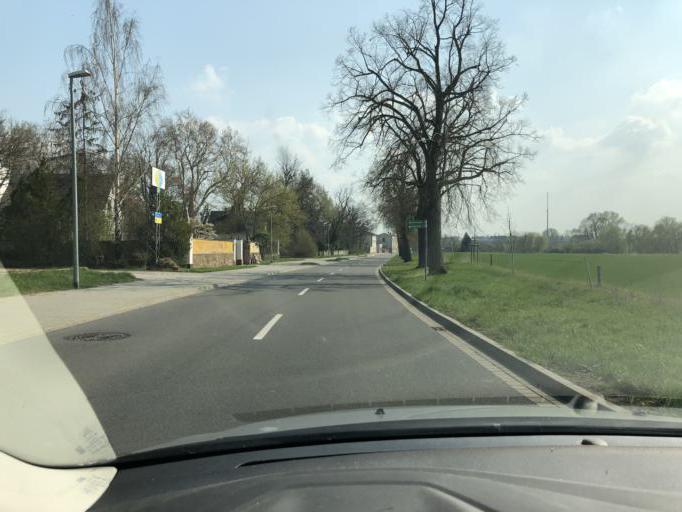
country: DE
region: Saxony-Anhalt
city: Grobers
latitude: 51.4389
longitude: 12.1168
